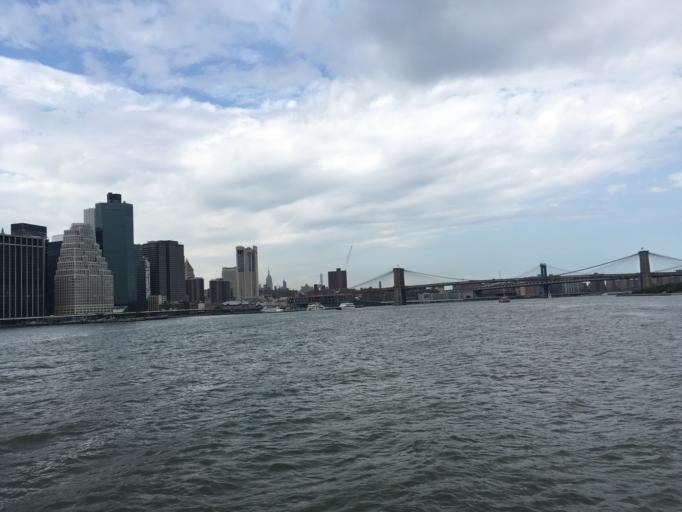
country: US
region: New York
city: New York City
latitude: 40.6969
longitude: -74.0060
